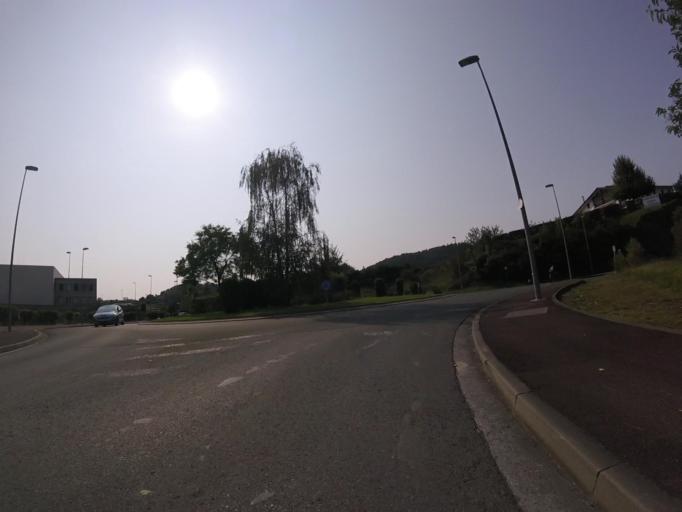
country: ES
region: Basque Country
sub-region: Provincia de Guipuzcoa
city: Errenteria
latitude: 43.2951
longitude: -1.8992
